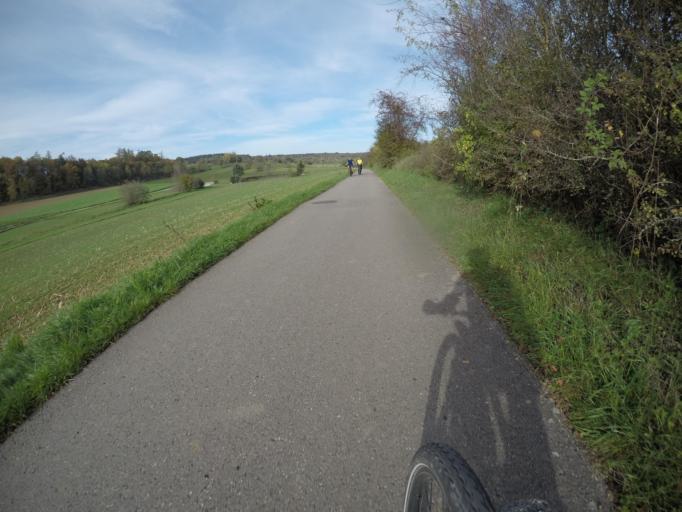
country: DE
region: Baden-Wuerttemberg
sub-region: Regierungsbezirk Stuttgart
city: Weil der Stadt
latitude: 48.7721
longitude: 8.8911
